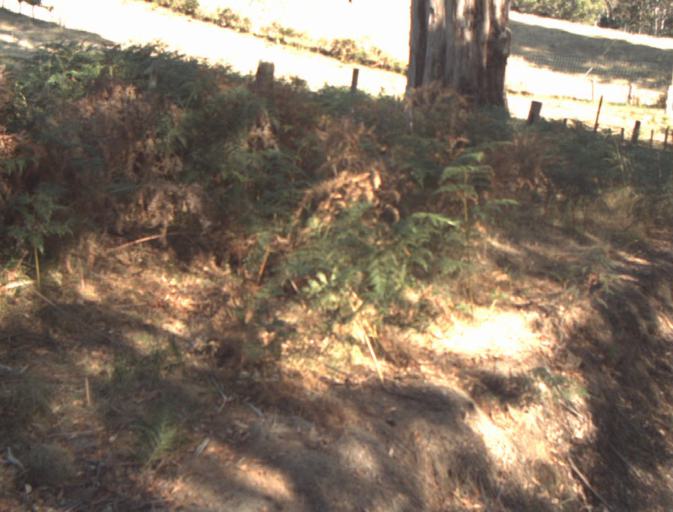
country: AU
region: Tasmania
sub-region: Launceston
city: Mayfield
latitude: -41.2960
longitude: 147.1988
